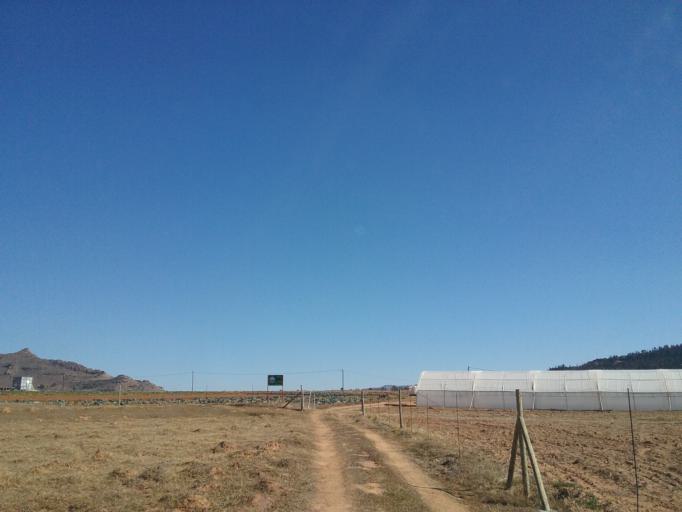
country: LS
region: Maseru
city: Nako
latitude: -29.4950
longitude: 27.5978
